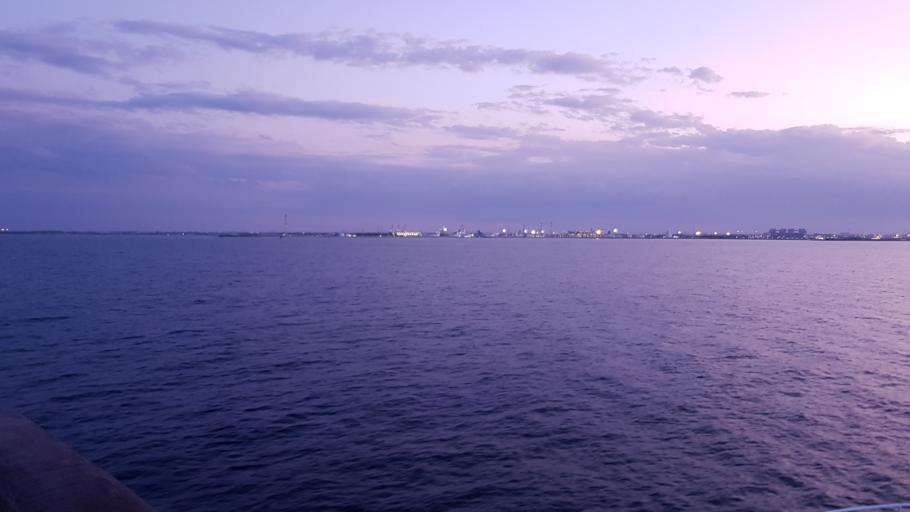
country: IT
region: Apulia
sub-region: Provincia di Brindisi
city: Materdomini
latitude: 40.6654
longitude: 18.0338
